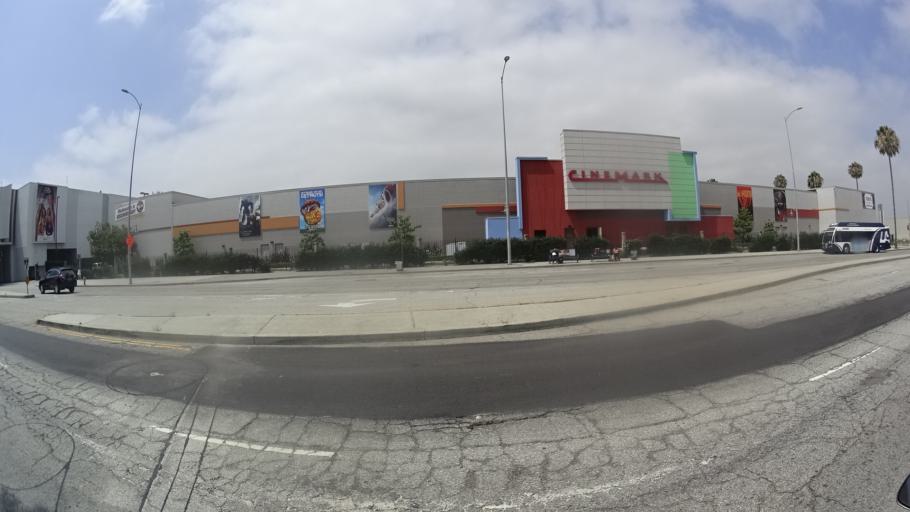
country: US
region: California
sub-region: Los Angeles County
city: View Park-Windsor Hills
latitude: 34.0118
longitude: -118.3370
